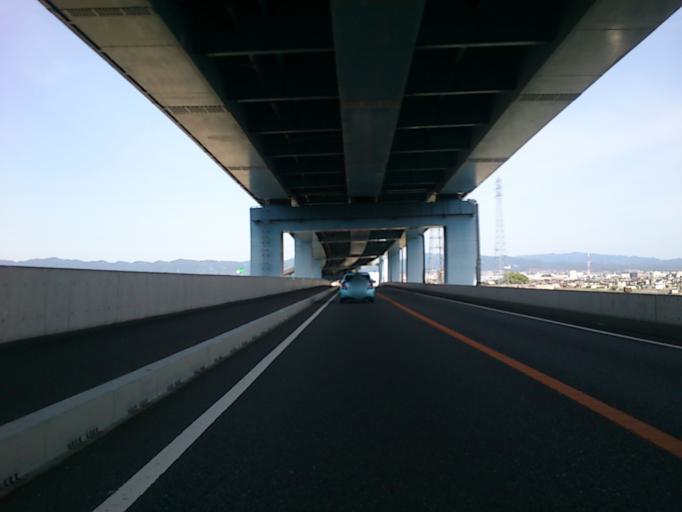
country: JP
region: Kyoto
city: Yawata
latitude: 34.8903
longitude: 135.7093
